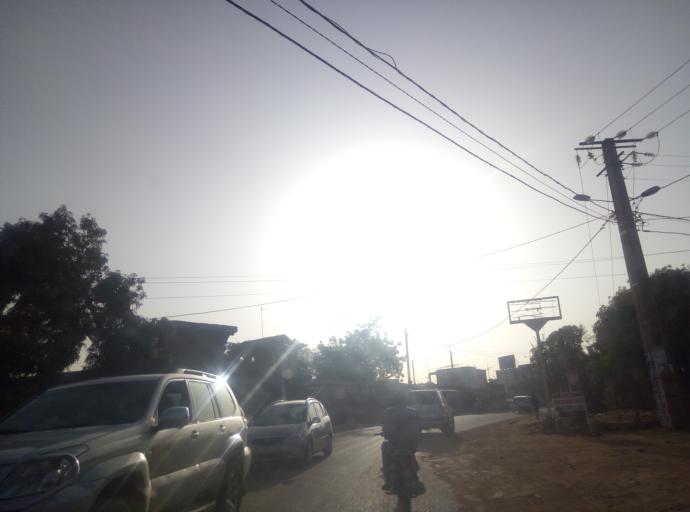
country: ML
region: Bamako
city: Bamako
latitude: 12.6112
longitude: -7.9752
